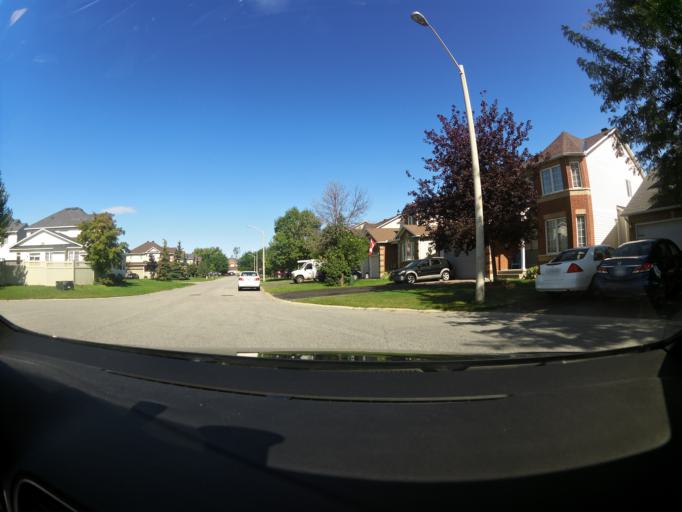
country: CA
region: Ontario
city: Bells Corners
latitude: 45.2722
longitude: -75.9425
